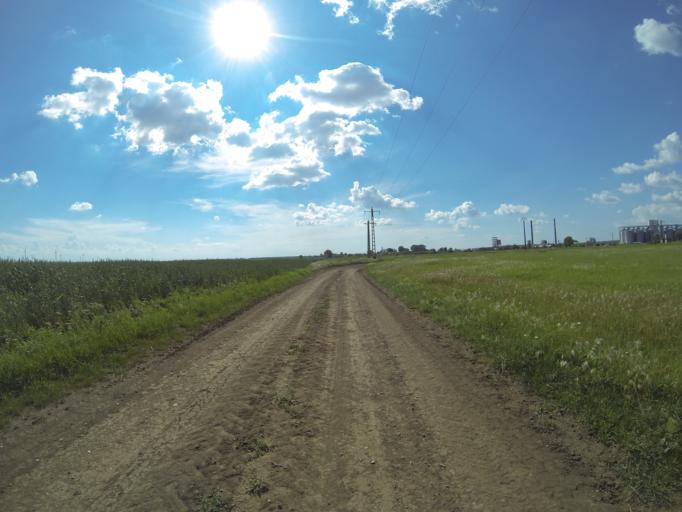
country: RO
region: Dolj
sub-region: Comuna Segarcea
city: Segarcea
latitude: 44.0791
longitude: 23.7328
